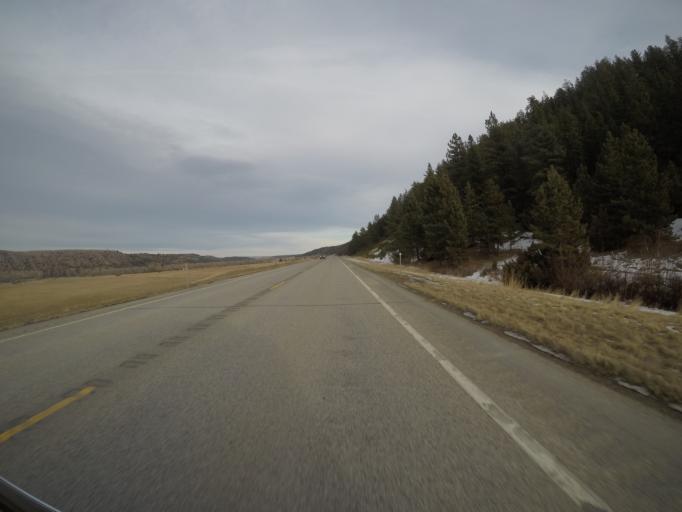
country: US
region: Montana
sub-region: Stillwater County
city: Absarokee
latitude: 45.5520
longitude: -109.3637
